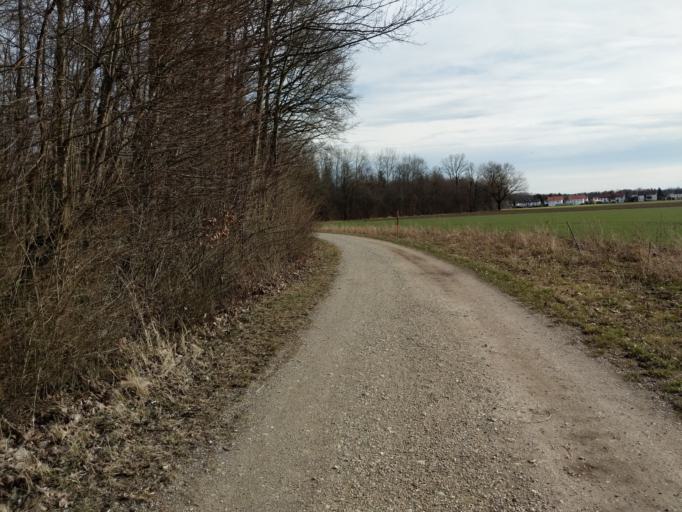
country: DE
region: Bavaria
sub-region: Upper Bavaria
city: Zorneding
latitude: 48.1002
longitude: 11.8372
